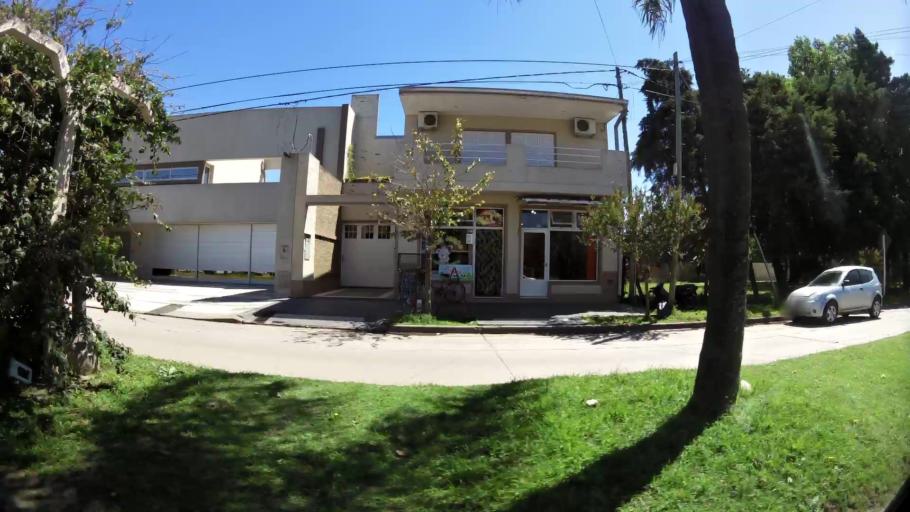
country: AR
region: Santa Fe
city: Esperanza
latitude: -31.4531
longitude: -60.9126
